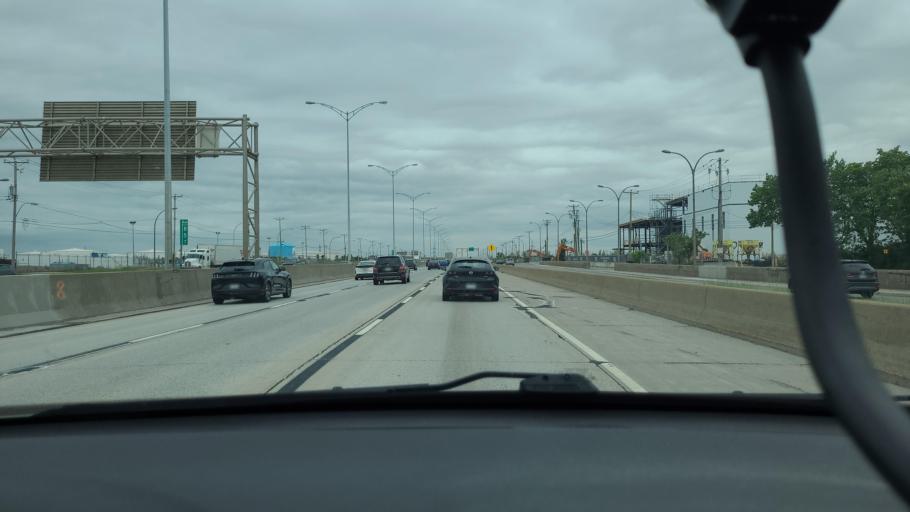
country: CA
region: Quebec
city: Montreal-Est
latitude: 45.6396
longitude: -73.5361
